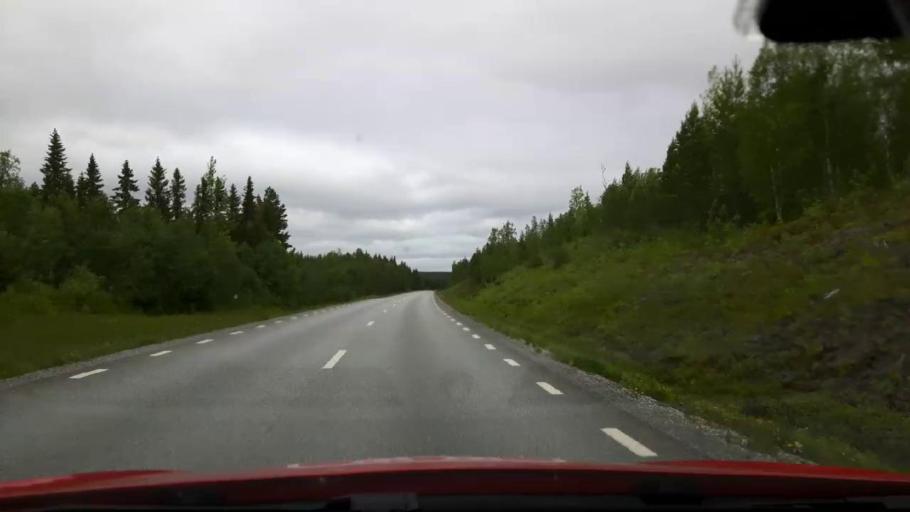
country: SE
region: Jaemtland
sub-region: OEstersunds Kommun
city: Lit
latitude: 63.7244
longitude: 14.7191
